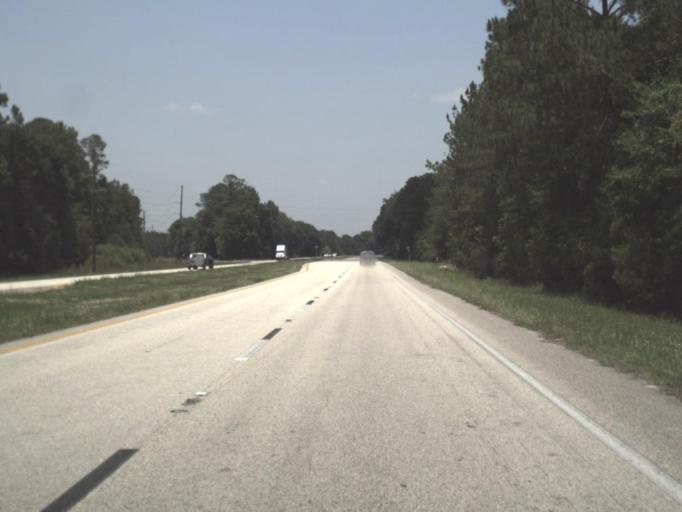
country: US
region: Florida
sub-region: Bradford County
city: Starke
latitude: 30.0159
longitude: -82.0867
